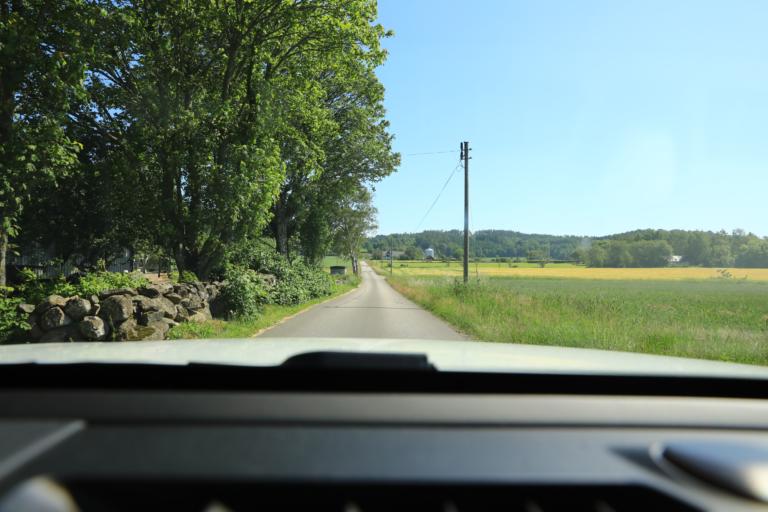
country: SE
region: Halland
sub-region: Varbergs Kommun
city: Veddige
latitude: 57.2058
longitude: 12.3177
